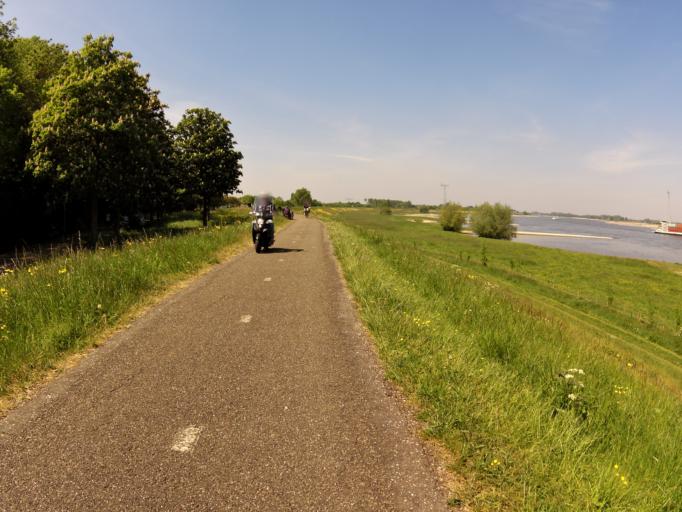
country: NL
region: Gelderland
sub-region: Gemeente Maasdriel
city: Heerewaarden
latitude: 51.8024
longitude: 5.3436
